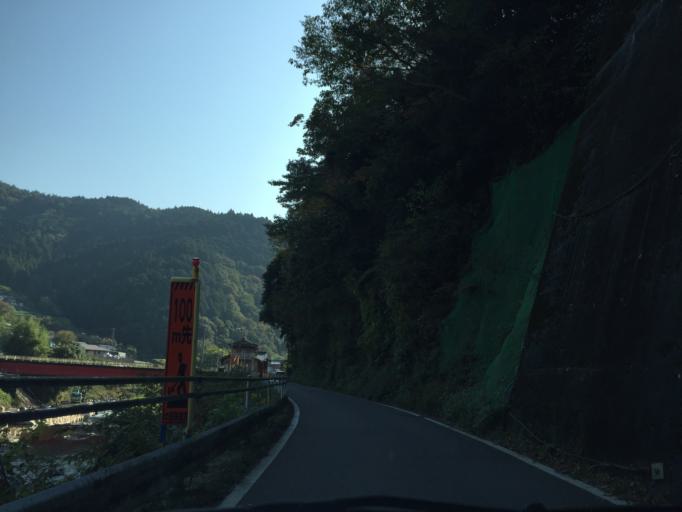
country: JP
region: Gifu
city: Minokamo
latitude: 35.5453
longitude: 137.1190
